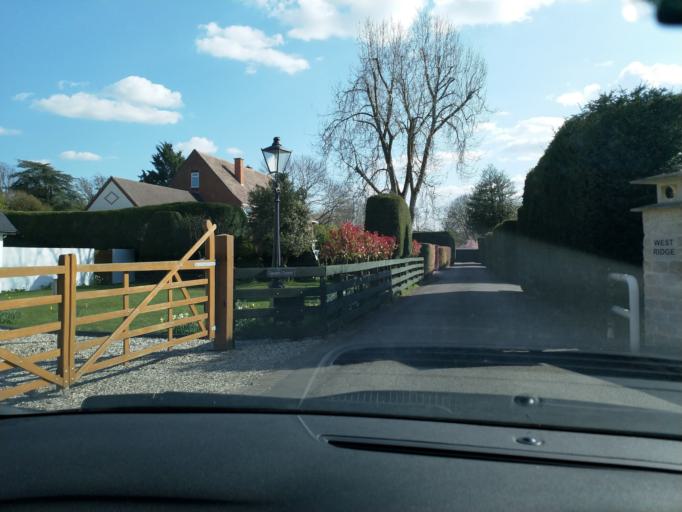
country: GB
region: England
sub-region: Warwickshire
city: Wellesbourne Mountford
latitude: 52.1873
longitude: -1.5551
